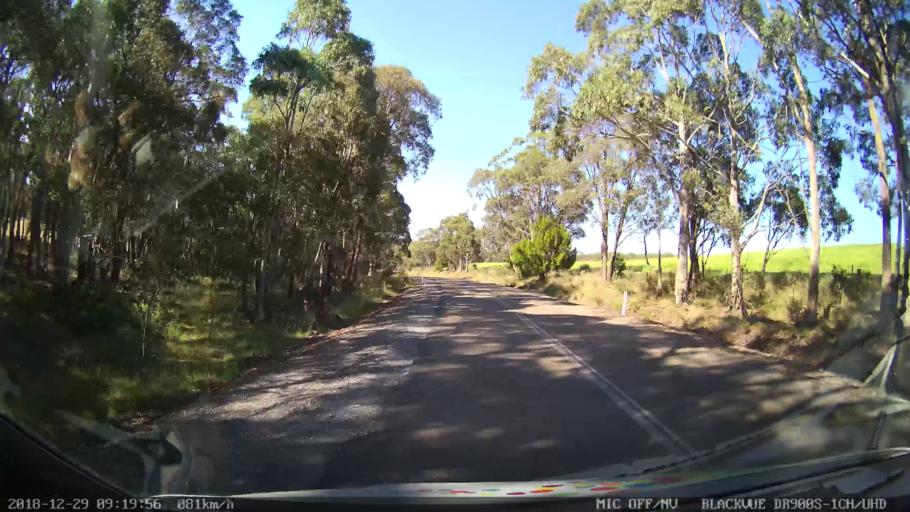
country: AU
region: New South Wales
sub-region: Upper Lachlan Shire
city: Crookwell
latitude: -34.4862
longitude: 149.4250
